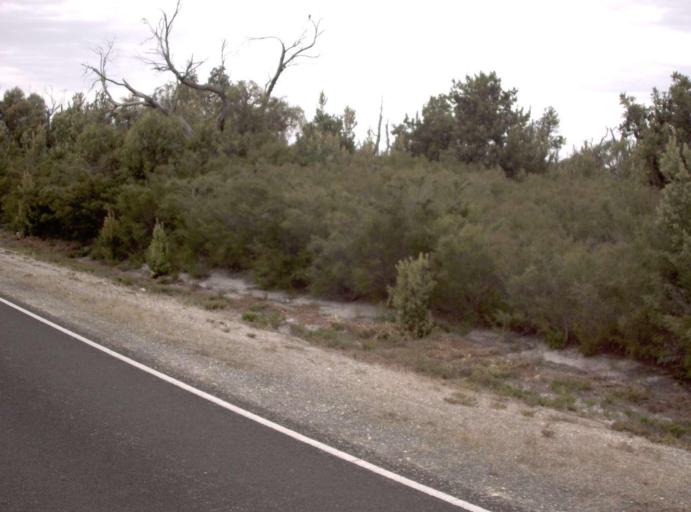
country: AU
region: Victoria
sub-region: Wellington
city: Sale
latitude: -38.1927
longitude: 147.3654
